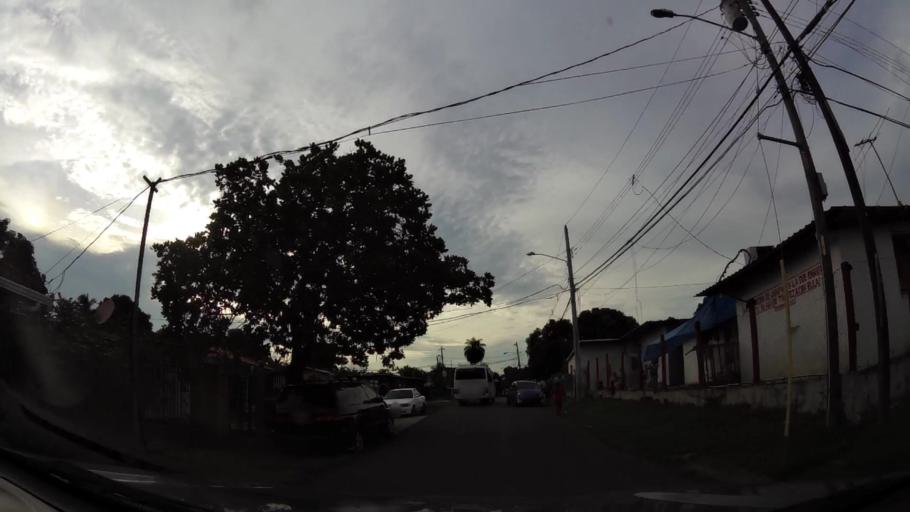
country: PA
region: Panama
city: Tocumen
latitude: 9.0904
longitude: -79.3817
